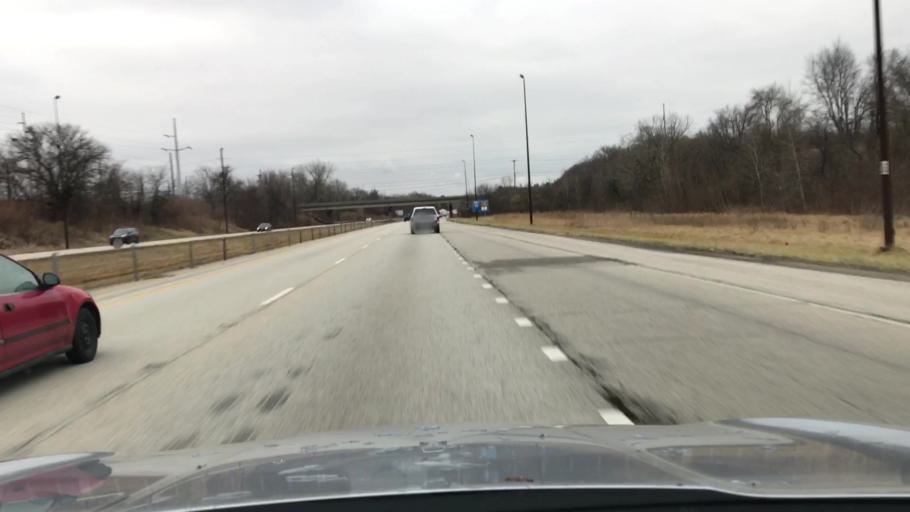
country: US
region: Illinois
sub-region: Sangamon County
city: Grandview
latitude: 39.8266
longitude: -89.5929
